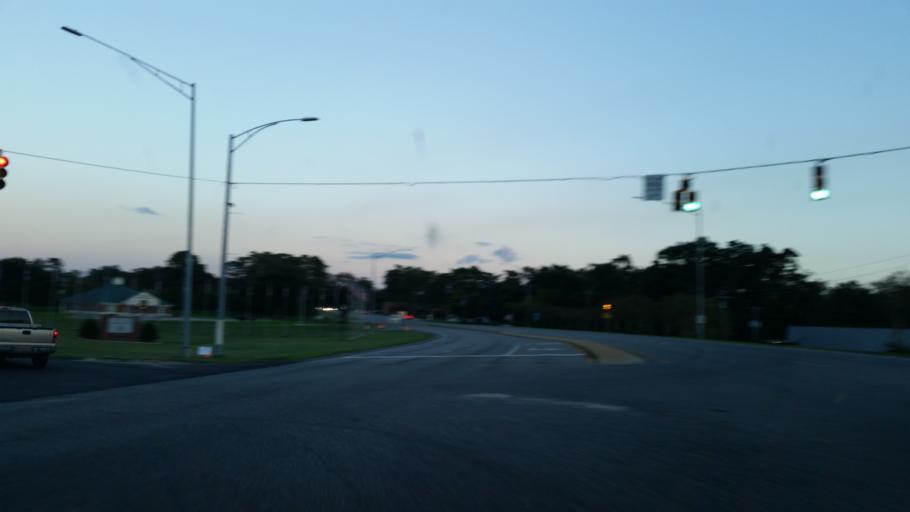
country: US
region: Alabama
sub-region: Baldwin County
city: Robertsdale
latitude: 30.5639
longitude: -87.7188
